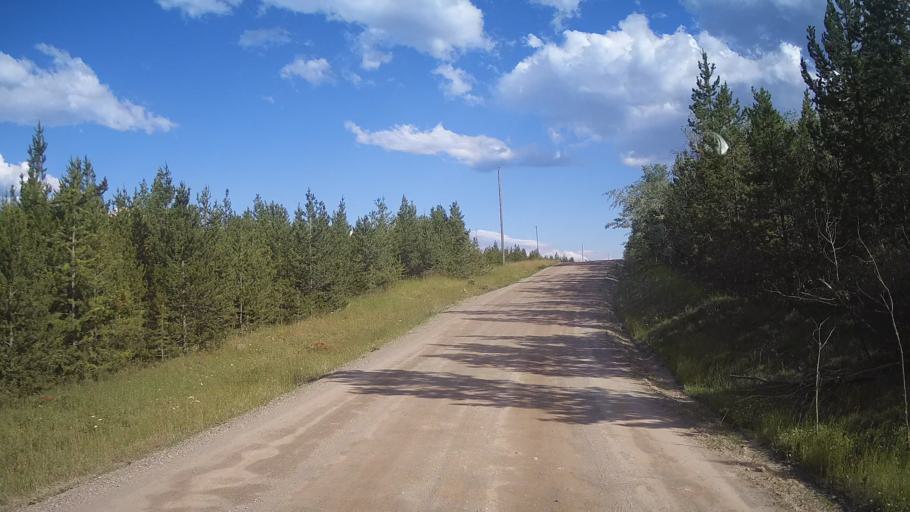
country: CA
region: British Columbia
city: Cache Creek
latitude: 51.2816
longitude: -121.7379
